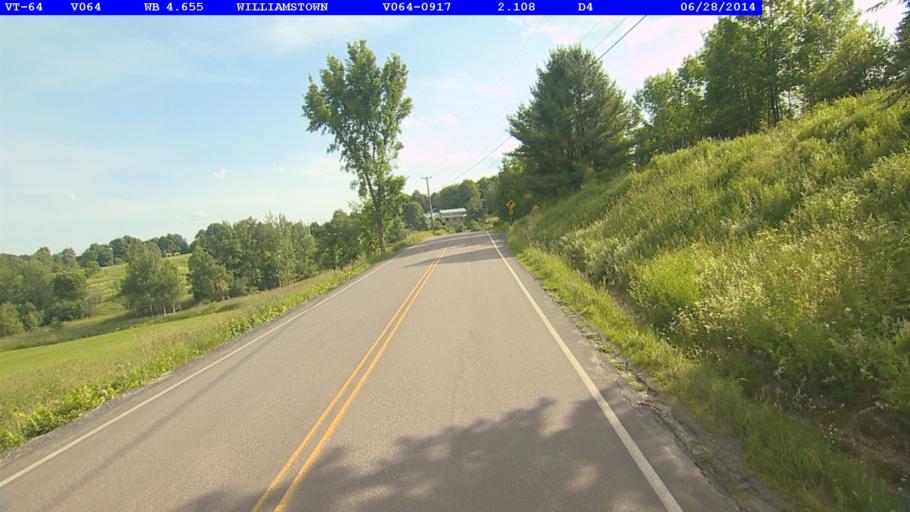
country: US
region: Vermont
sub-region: Orange County
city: Williamstown
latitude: 44.1141
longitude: -72.5757
